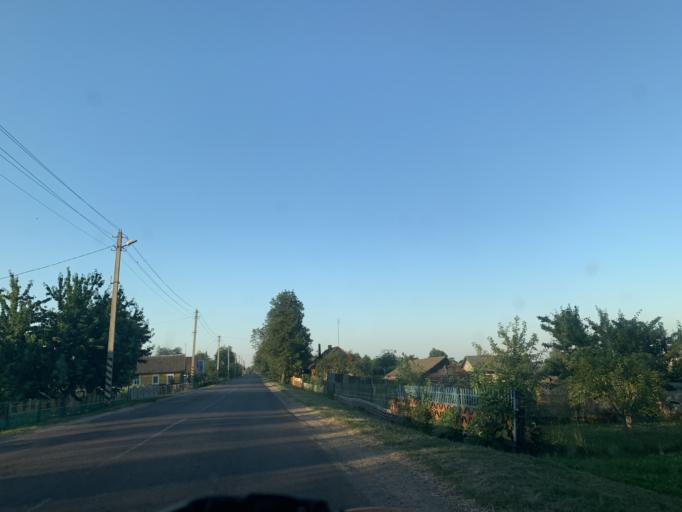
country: BY
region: Minsk
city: Haradzyeya
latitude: 53.2448
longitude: 26.5068
